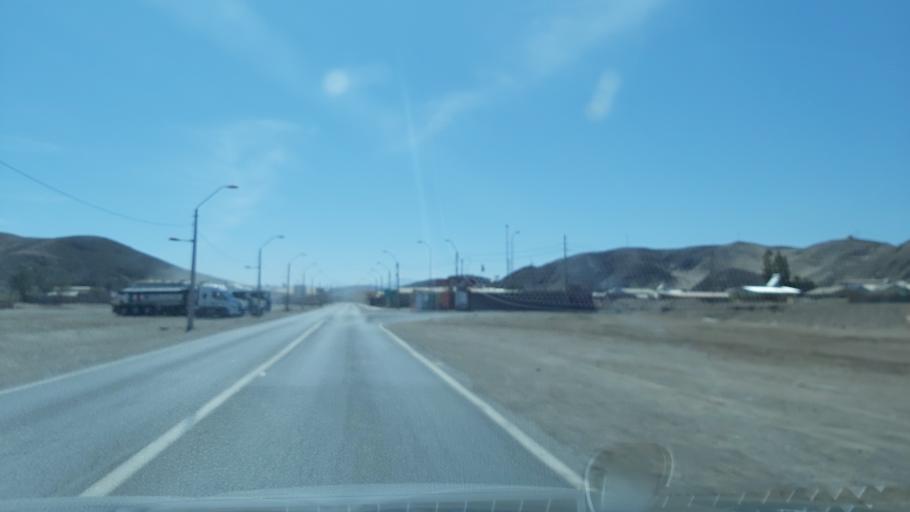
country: CL
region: Atacama
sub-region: Provincia de Chanaral
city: Diego de Almagro
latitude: -26.3917
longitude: -70.0417
